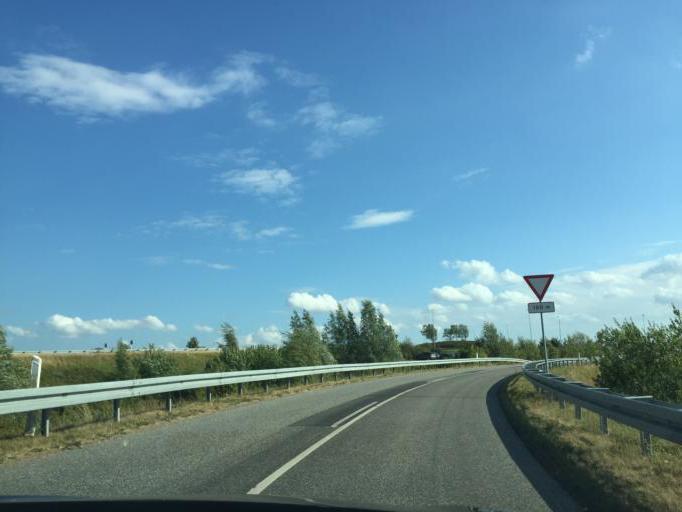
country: DK
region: South Denmark
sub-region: Faaborg-Midtfyn Kommune
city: Arslev
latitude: 55.3067
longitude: 10.4340
